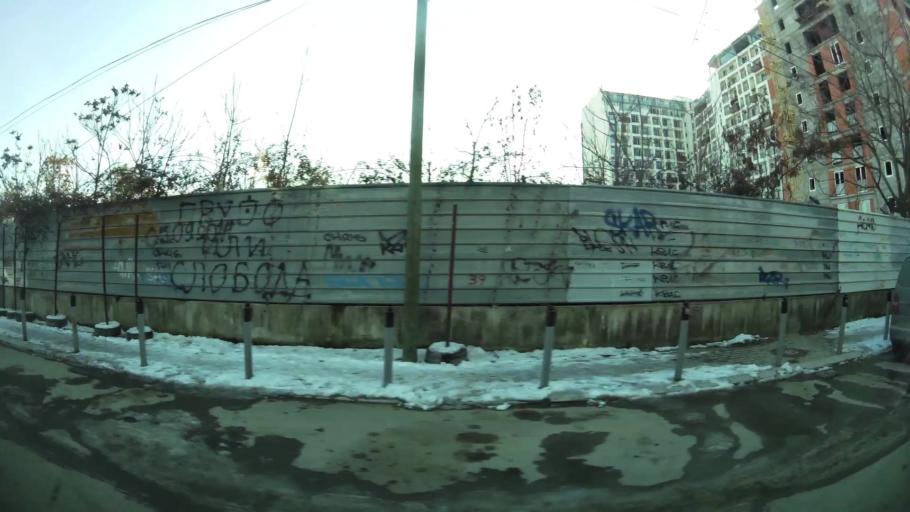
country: MK
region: Karpos
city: Skopje
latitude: 41.9984
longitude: 21.3992
